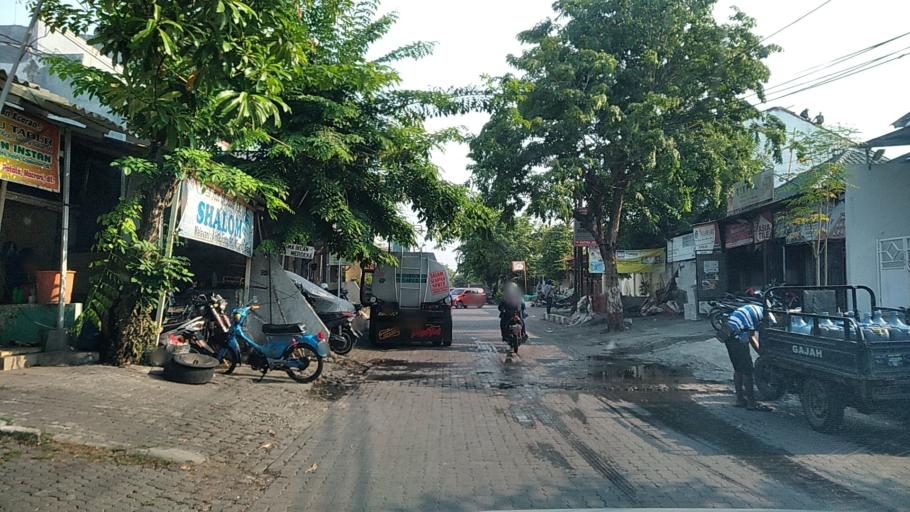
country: ID
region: Central Java
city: Semarang
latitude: -6.9580
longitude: 110.4046
